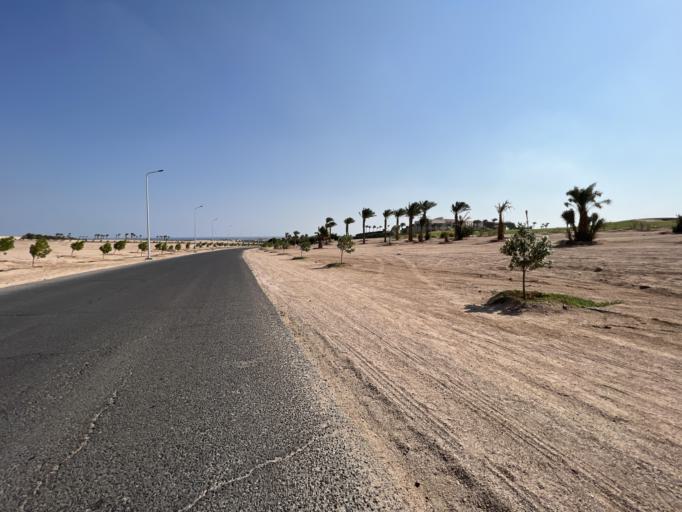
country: EG
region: Red Sea
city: Makadi Bay
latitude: 26.9855
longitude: 33.8851
